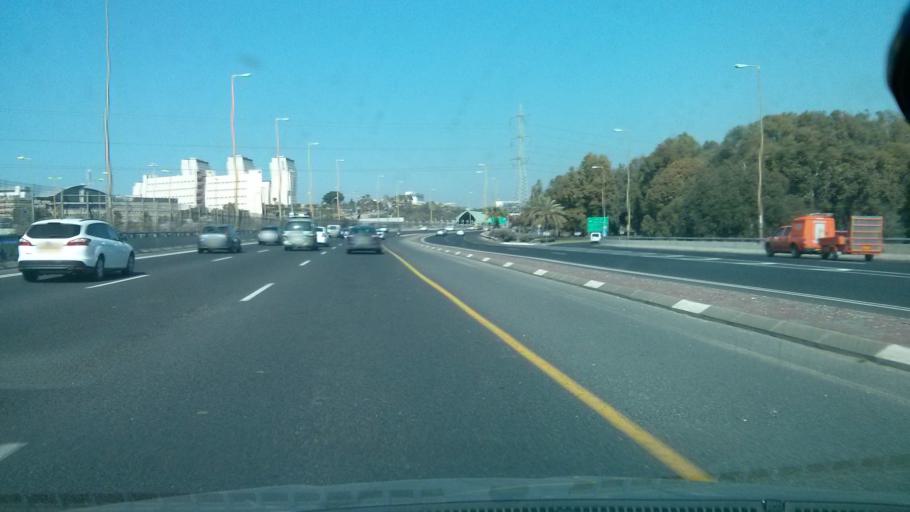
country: IL
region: Tel Aviv
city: Ramat Gan
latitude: 32.0992
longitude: 34.8029
